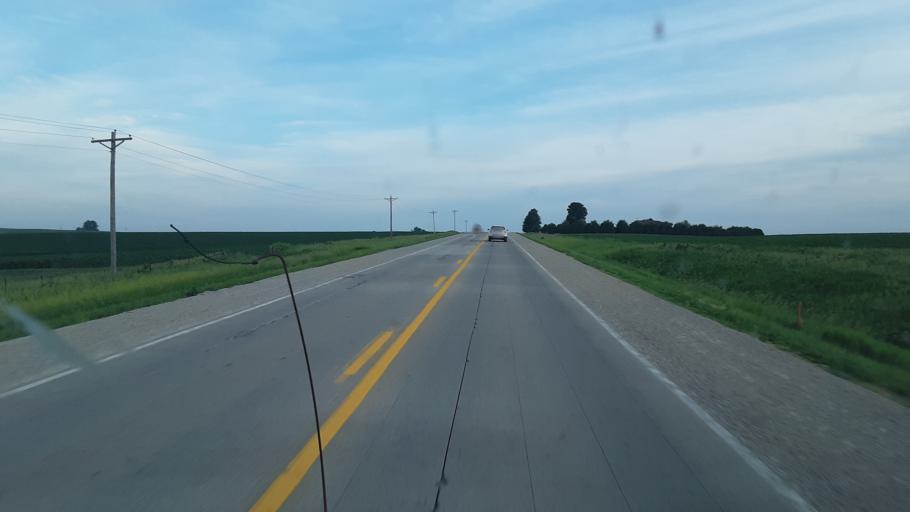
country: US
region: Iowa
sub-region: Benton County
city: Belle Plaine
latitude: 41.8055
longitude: -92.2789
